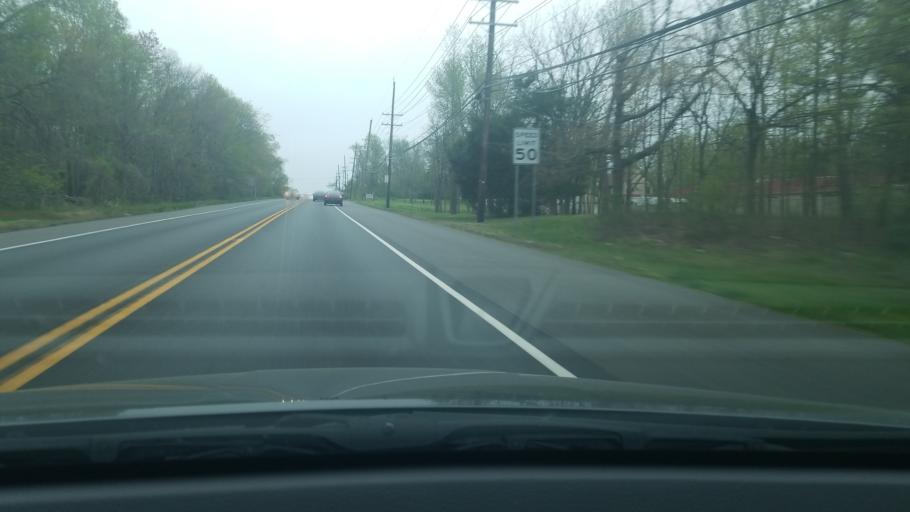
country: US
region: New Jersey
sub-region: Burlington County
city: Medford Lakes
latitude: 39.9044
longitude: -74.8117
